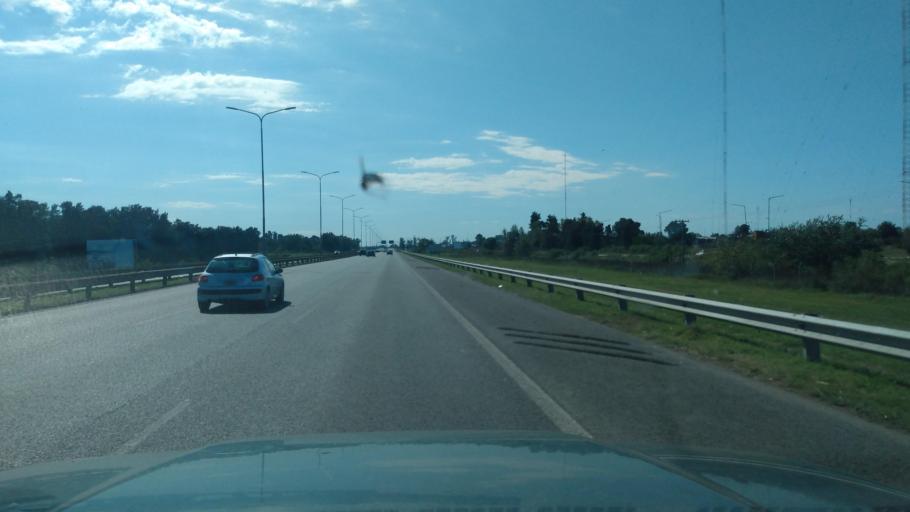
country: AR
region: Buenos Aires
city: Hurlingham
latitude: -34.5427
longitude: -58.6016
